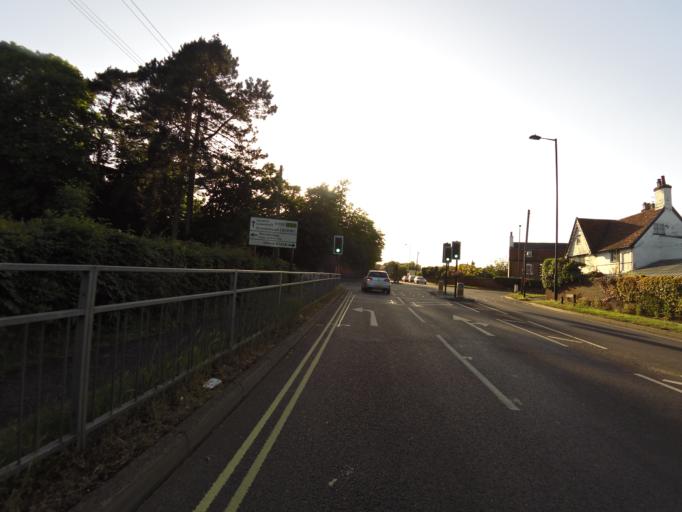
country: GB
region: England
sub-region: Suffolk
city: Woodbridge
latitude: 52.1047
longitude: 1.3304
